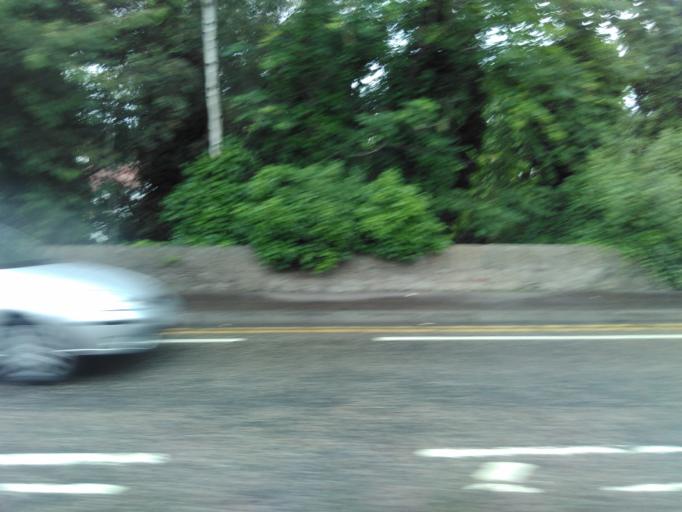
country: GB
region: Scotland
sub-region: Edinburgh
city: Edinburgh
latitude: 55.9238
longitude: -3.1657
